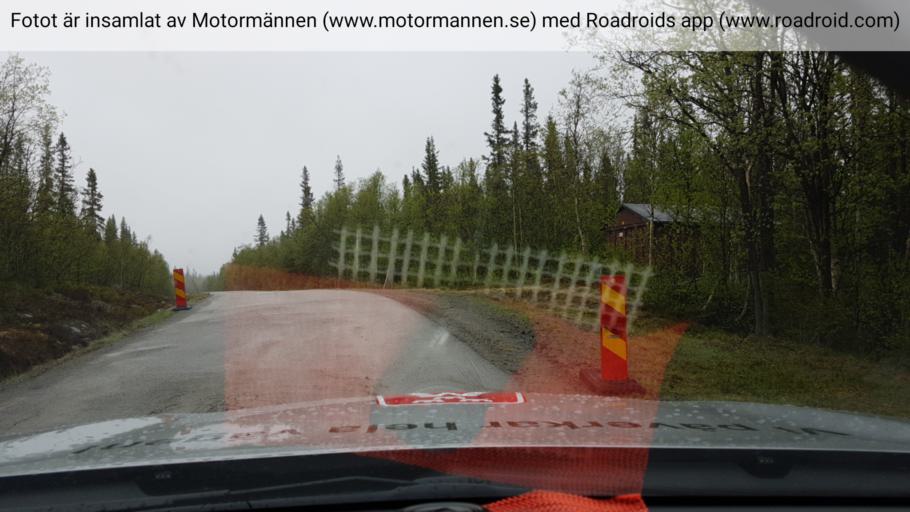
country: SE
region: Jaemtland
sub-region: Bergs Kommun
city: Hoverberg
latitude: 63.0051
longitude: 13.9457
